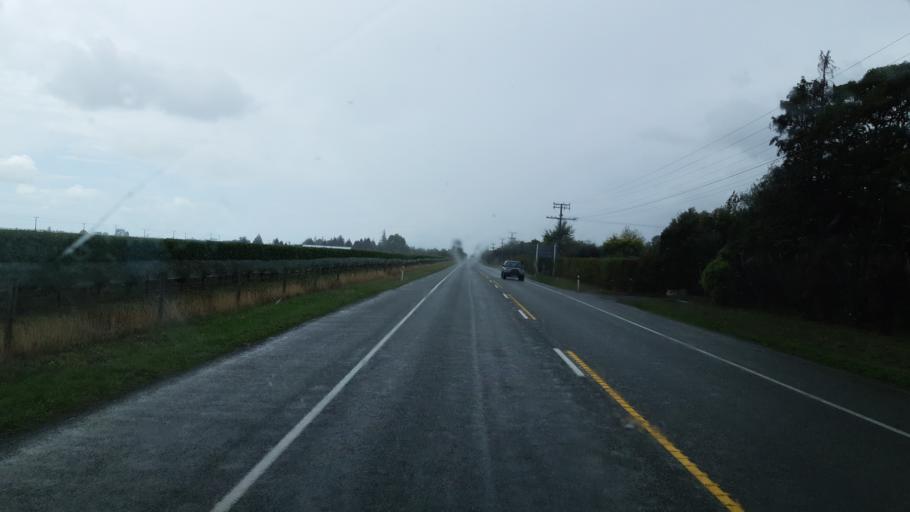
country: NZ
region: Tasman
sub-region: Tasman District
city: Brightwater
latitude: -41.3621
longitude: 173.1411
